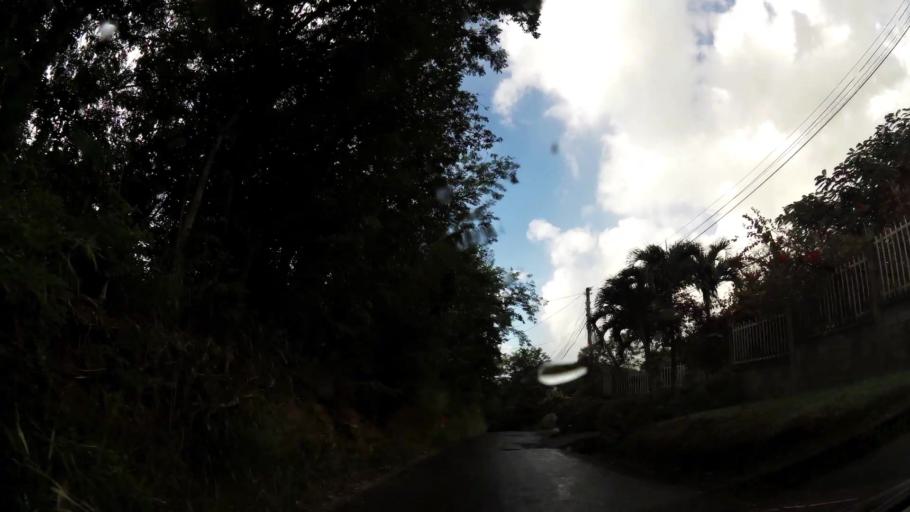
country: DM
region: Saint George
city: Roseau
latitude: 15.3267
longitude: -61.3917
